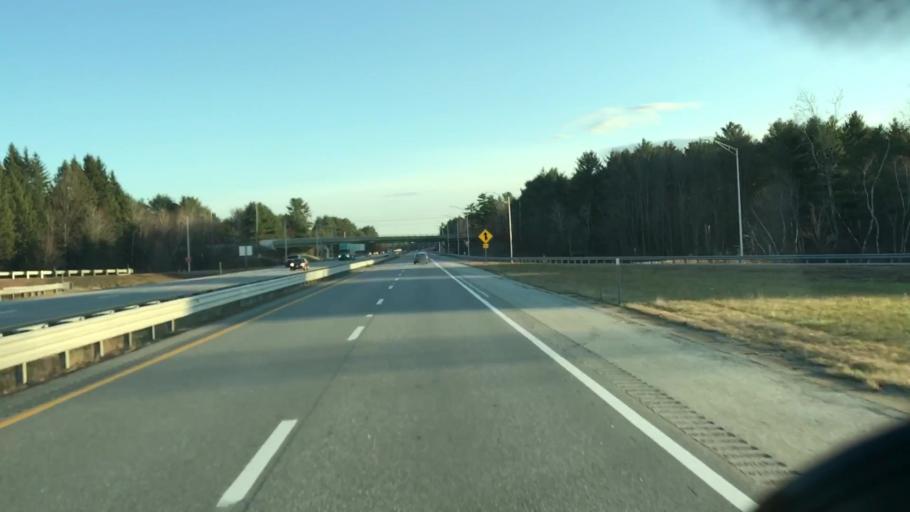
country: US
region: Maine
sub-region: Cumberland County
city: New Gloucester
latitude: 43.8809
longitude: -70.3347
